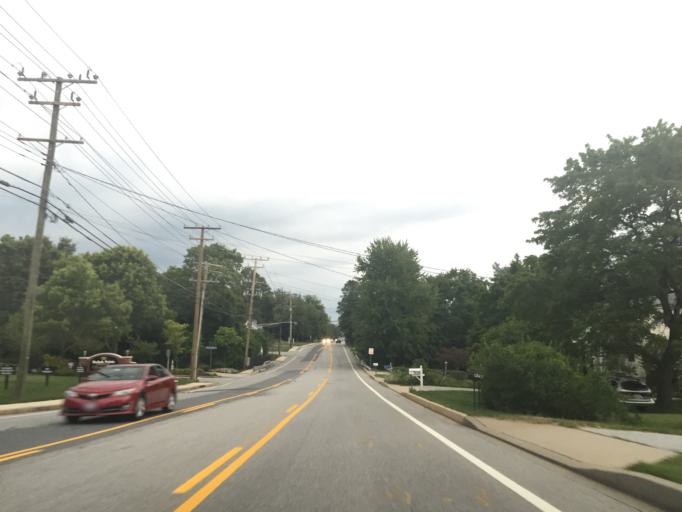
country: US
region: Maryland
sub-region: Baltimore County
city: Carney
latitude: 39.3984
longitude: -76.5208
